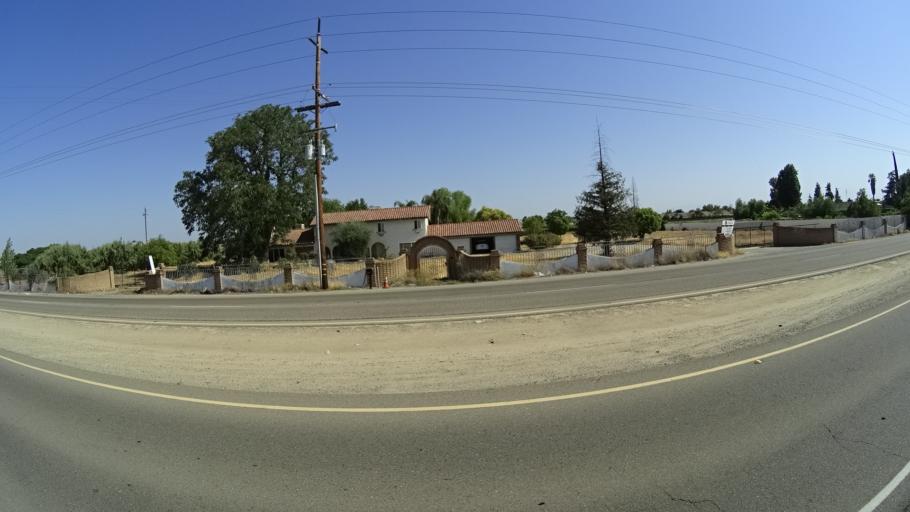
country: US
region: California
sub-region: Fresno County
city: Sunnyside
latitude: 36.7074
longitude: -119.7063
